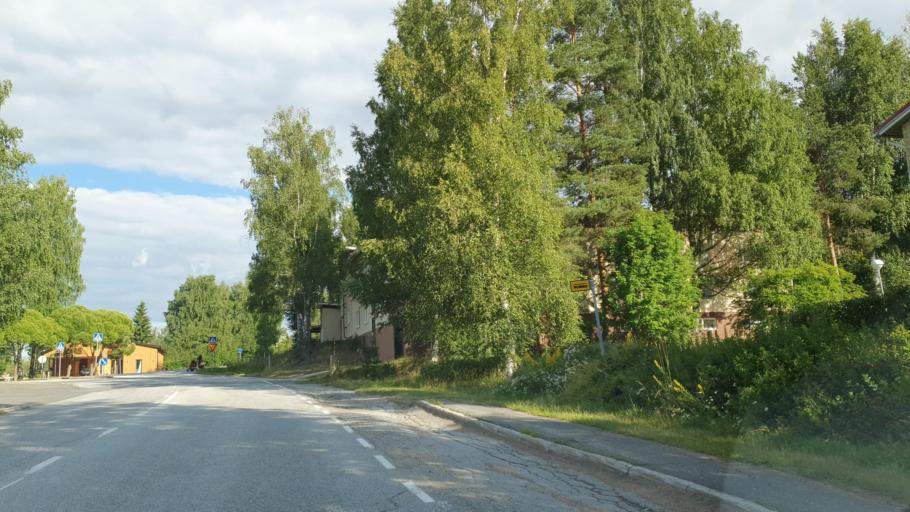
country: FI
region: Central Finland
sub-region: Jyvaeskylae
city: Saeynaetsalo
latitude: 62.1558
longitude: 25.7563
